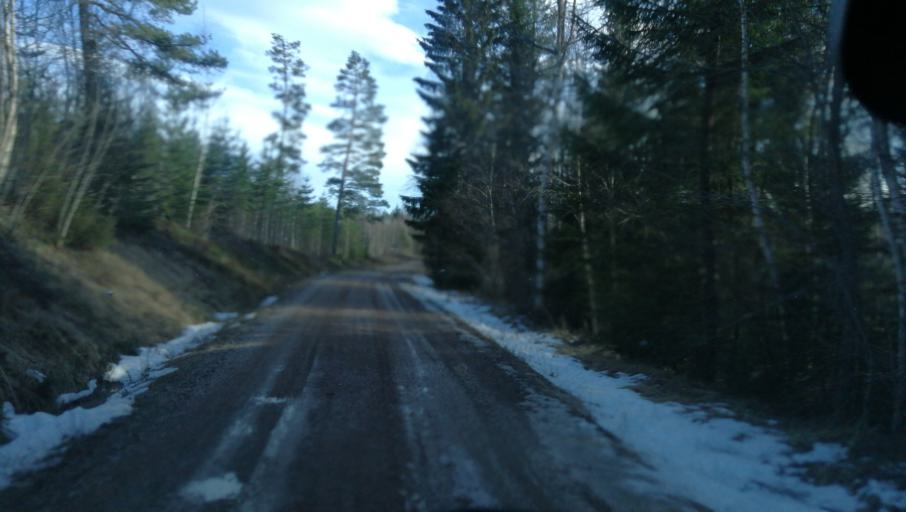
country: SE
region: Dalarna
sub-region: Vansbro Kommun
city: Vansbro
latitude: 60.8193
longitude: 14.1968
